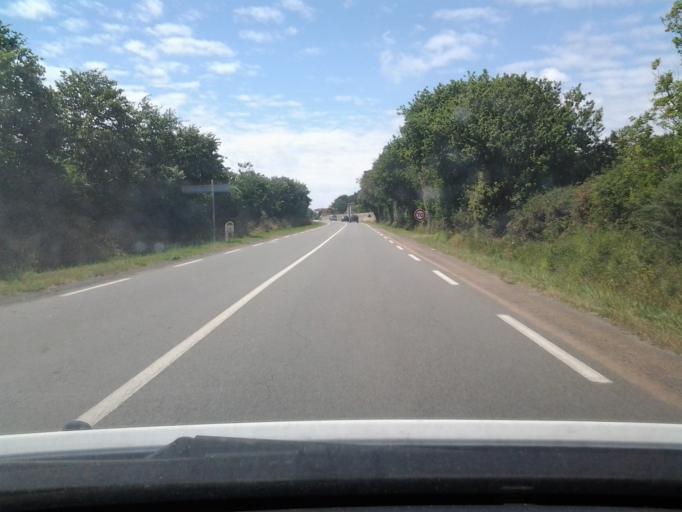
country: FR
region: Pays de la Loire
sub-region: Departement de la Vendee
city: Chateau-d'Olonne
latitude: 46.5266
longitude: -1.7467
